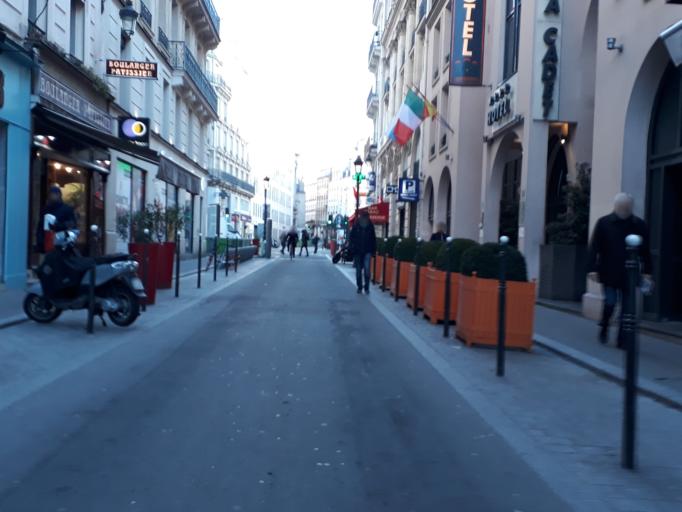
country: FR
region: Ile-de-France
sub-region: Paris
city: Paris
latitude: 48.8752
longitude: 2.3432
